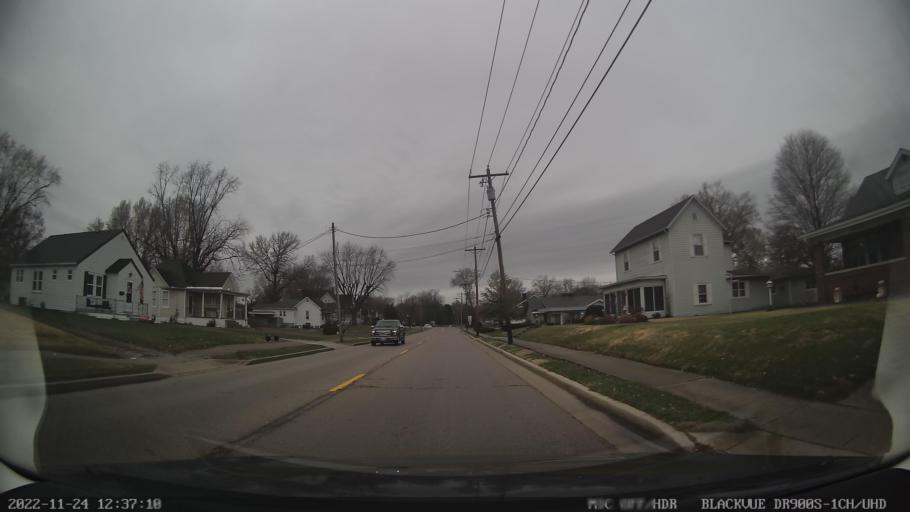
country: US
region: Illinois
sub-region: Macoupin County
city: Staunton
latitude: 39.0112
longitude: -89.7942
